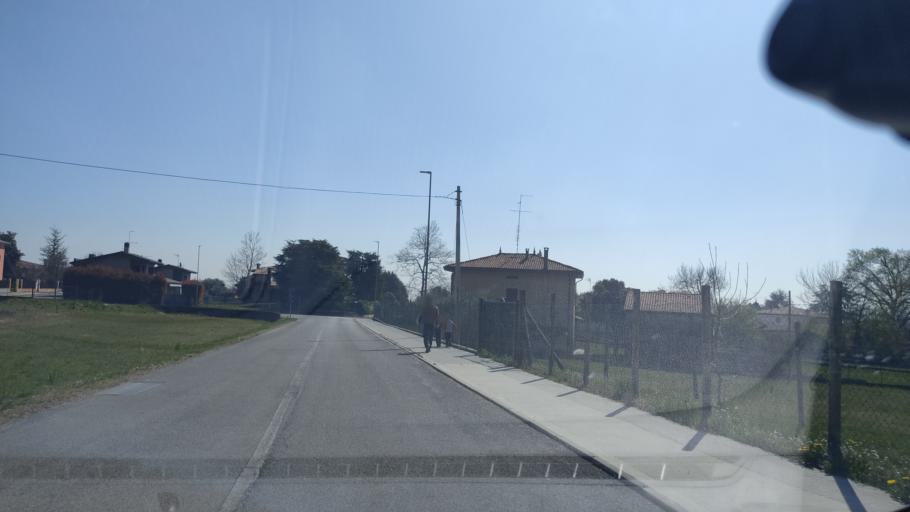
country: IT
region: Friuli Venezia Giulia
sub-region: Provincia di Pordenone
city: Budoia
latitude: 46.0397
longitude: 12.5346
